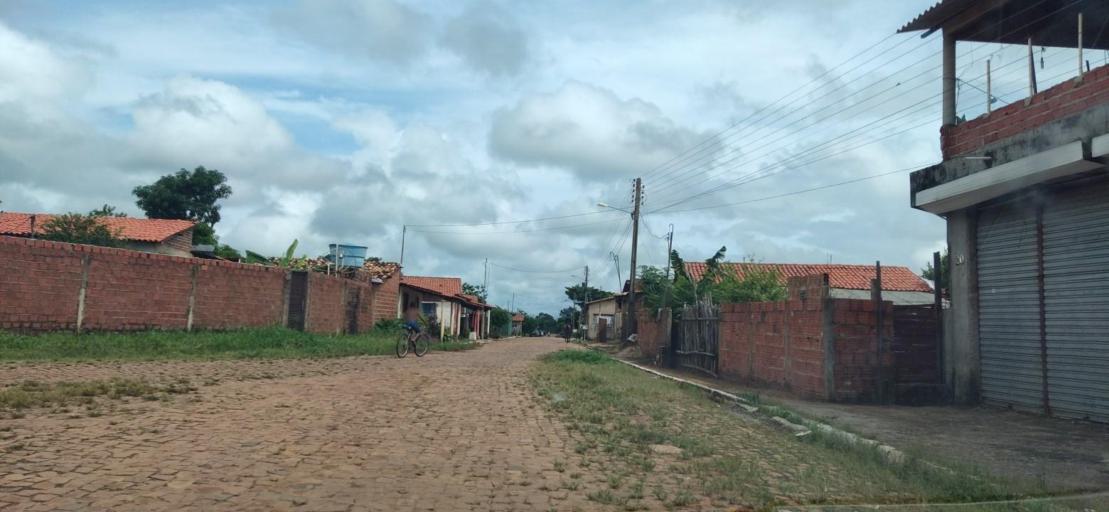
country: BR
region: Piaui
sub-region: Valenca Do Piaui
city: Valenca do Piaui
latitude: -6.1110
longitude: -41.7966
